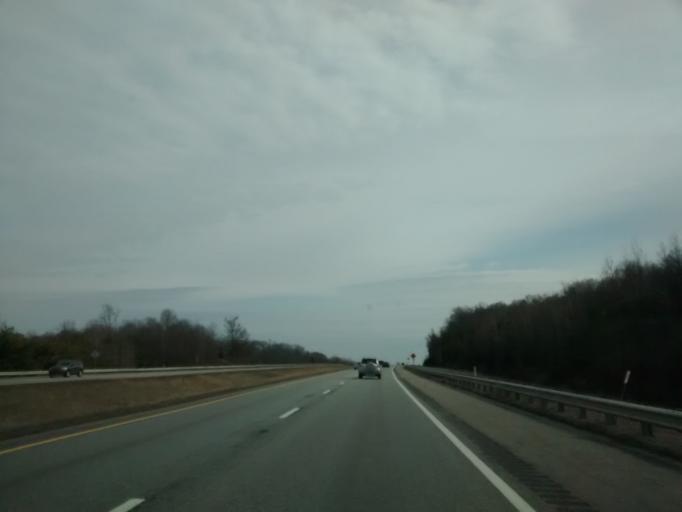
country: US
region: Massachusetts
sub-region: Worcester County
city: Uxbridge
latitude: 42.0449
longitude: -71.6272
